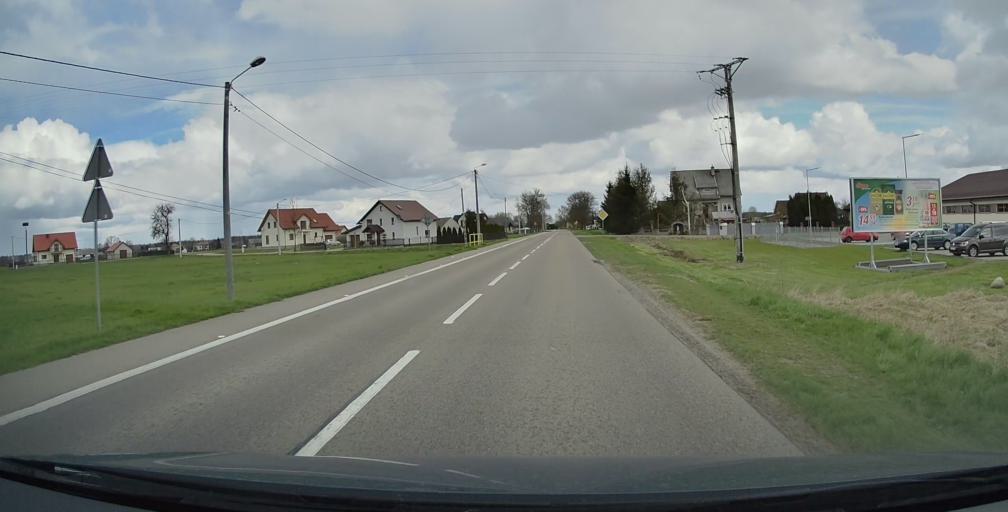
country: PL
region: Masovian Voivodeship
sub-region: Powiat ostrolecki
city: Rzekun
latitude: 52.9977
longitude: 21.5892
